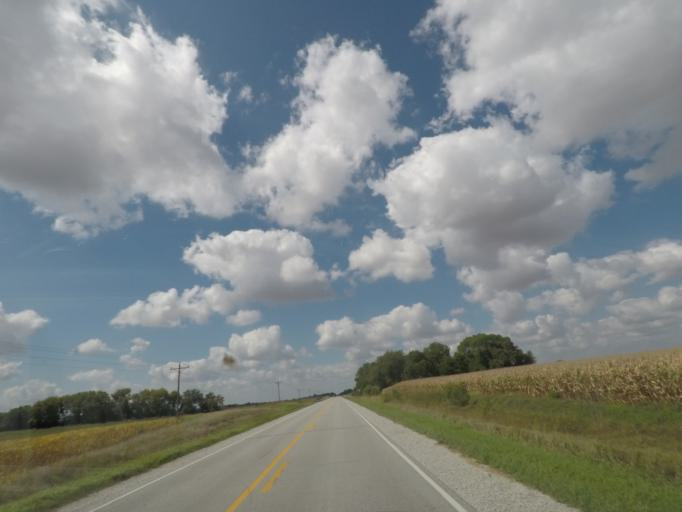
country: US
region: Iowa
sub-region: Story County
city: Nevada
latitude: 42.0226
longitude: -93.3500
